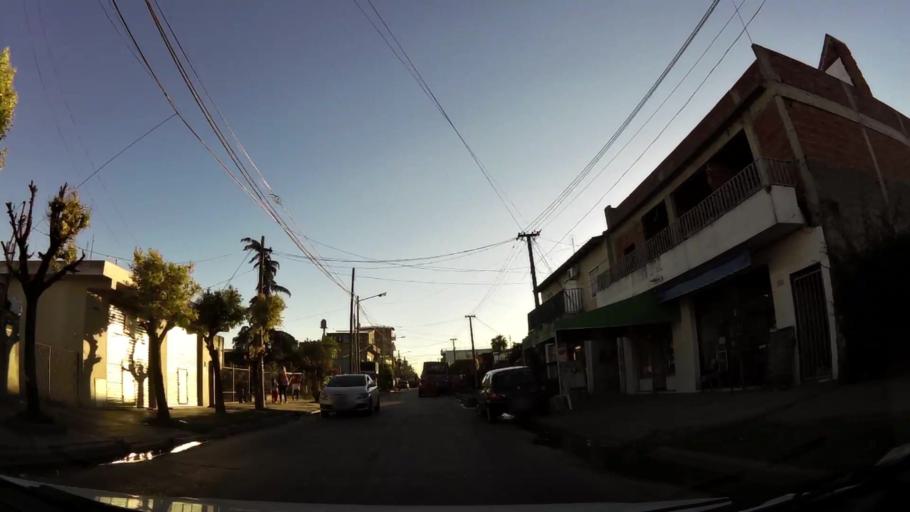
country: AR
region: Buenos Aires
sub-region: Partido de Moron
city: Moron
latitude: -34.7122
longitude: -58.6114
